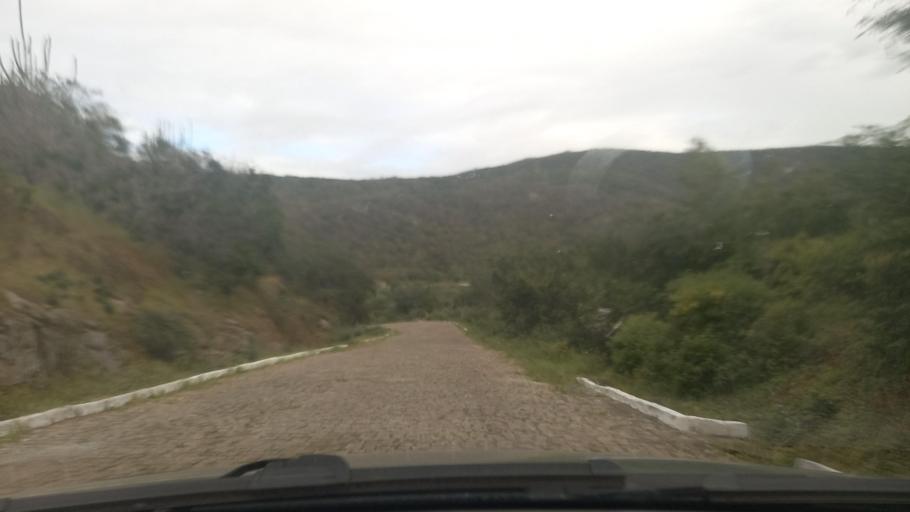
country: BR
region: Sergipe
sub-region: Caninde De Sao Francisco
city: Caninde de Sao Francisco
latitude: -9.6266
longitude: -37.8075
